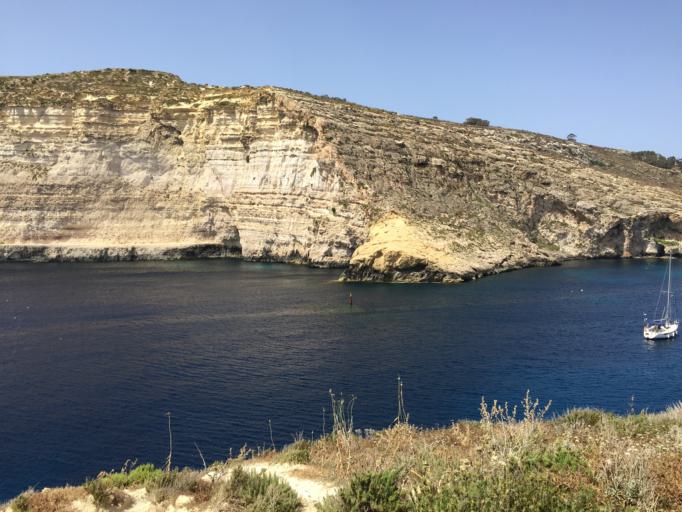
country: MT
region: Saint Lucia
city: Saint Lucia
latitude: 36.0277
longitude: 14.2133
